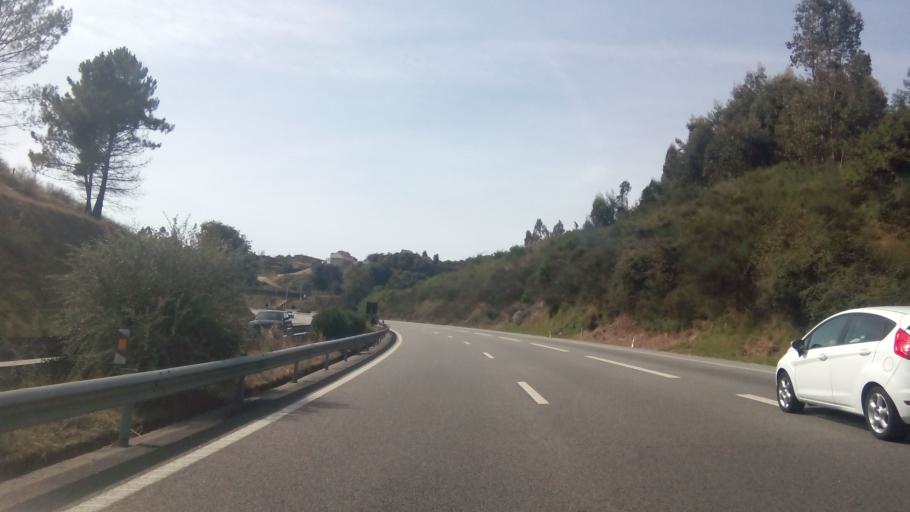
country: PT
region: Porto
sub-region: Lousada
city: Meinedo
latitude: 41.2323
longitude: -8.2198
